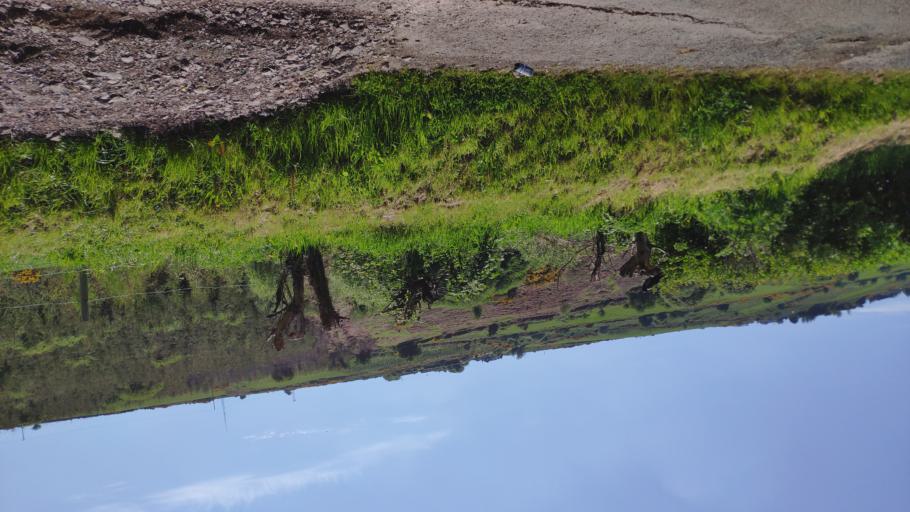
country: IE
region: Munster
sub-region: County Cork
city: Cork
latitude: 51.9176
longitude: -8.5120
